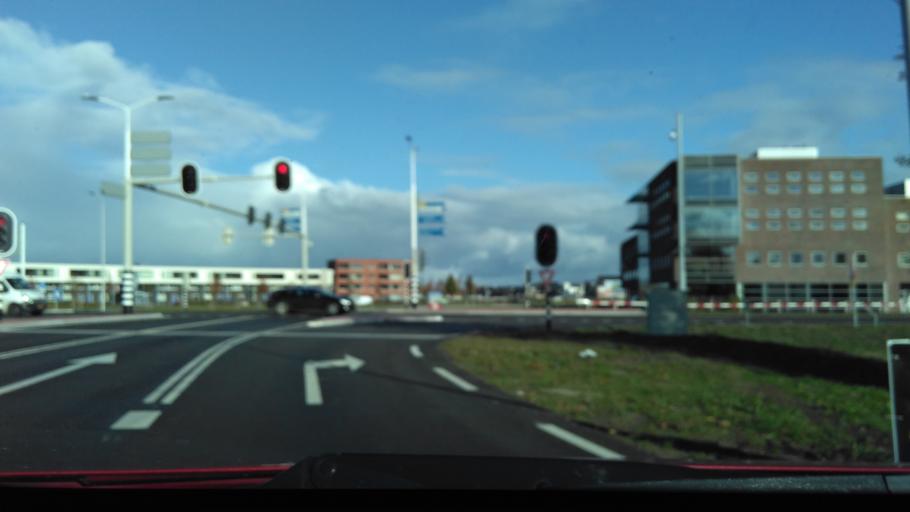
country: NL
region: Gelderland
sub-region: Gemeente Zaltbommel
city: Zaltbommel
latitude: 51.7947
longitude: 5.2492
